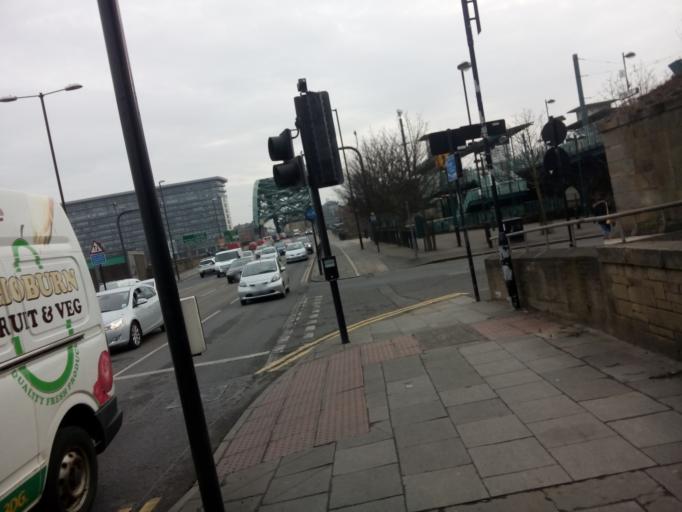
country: GB
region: England
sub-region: Sunderland
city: Sunderland
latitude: 54.9116
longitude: -1.3834
